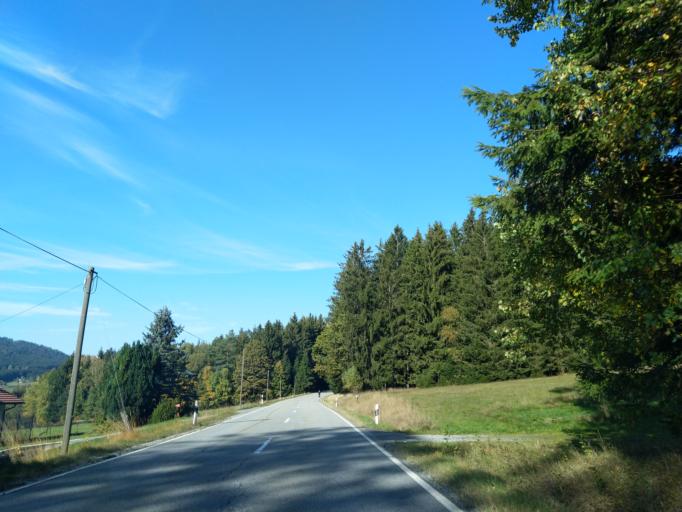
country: DE
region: Bavaria
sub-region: Lower Bavaria
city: Achslach
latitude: 48.9601
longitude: 12.9272
